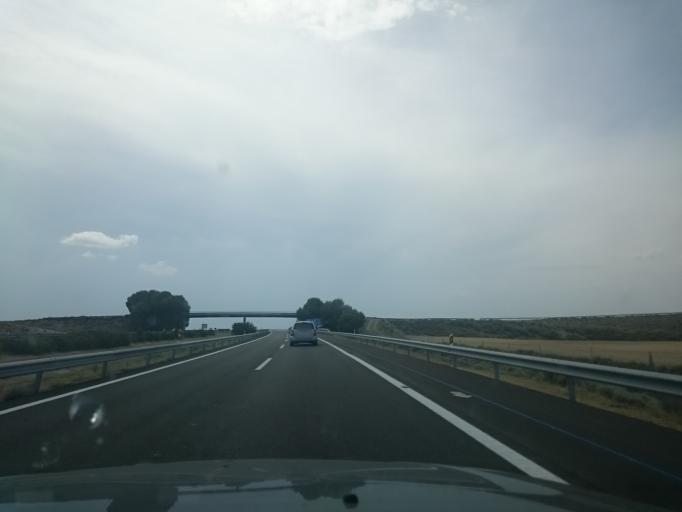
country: ES
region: Aragon
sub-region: Provincia de Zaragoza
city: Bujaraloz
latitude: 41.5263
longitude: -0.1932
